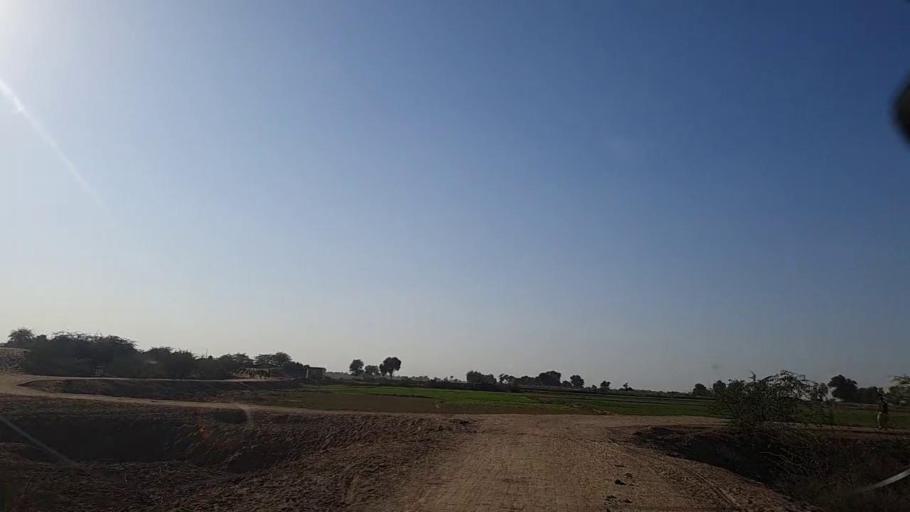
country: PK
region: Sindh
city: Khanpur
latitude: 27.7697
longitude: 69.2911
